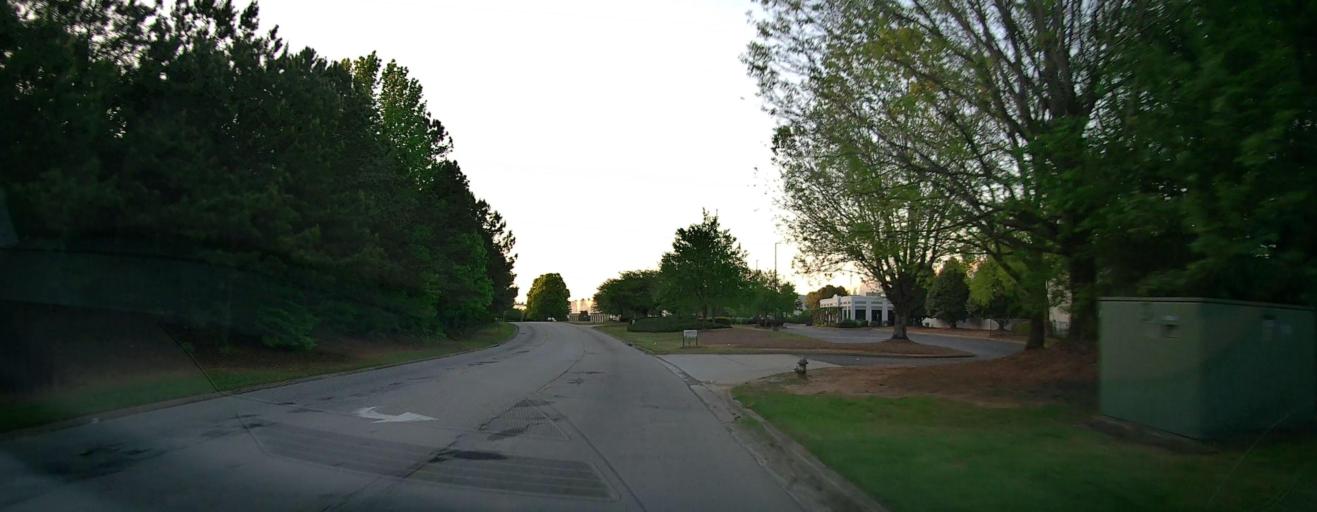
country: US
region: Georgia
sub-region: Henry County
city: McDonough
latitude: 33.4072
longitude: -84.1496
